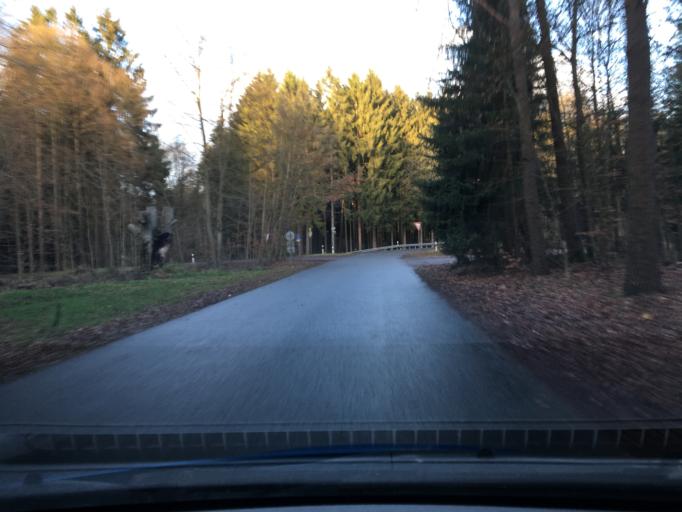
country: DE
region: Lower Saxony
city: Soderstorf
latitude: 53.0989
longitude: 10.1546
